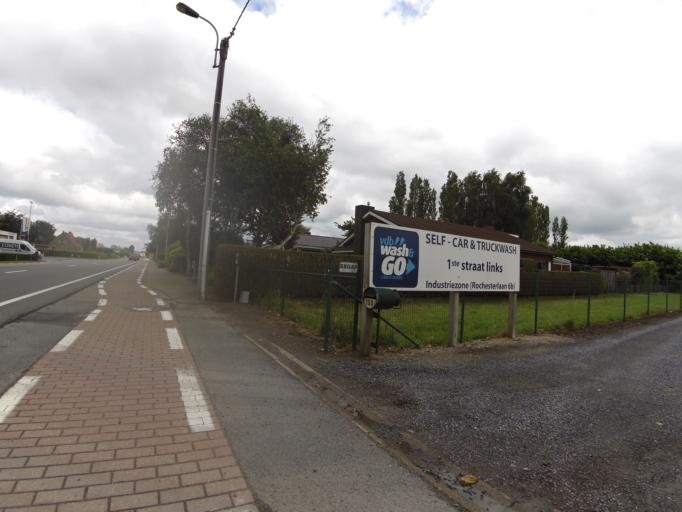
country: BE
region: Flanders
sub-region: Provincie West-Vlaanderen
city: Gistel
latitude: 51.1450
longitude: 2.9462
